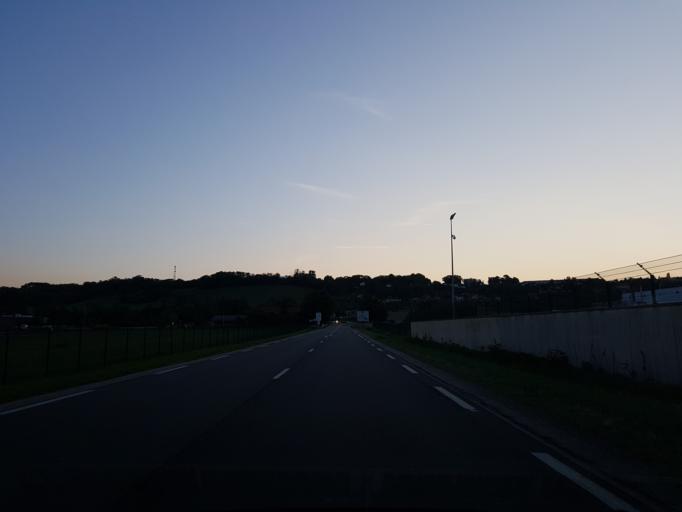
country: FR
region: Champagne-Ardenne
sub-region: Departement de la Haute-Marne
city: Langres
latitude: 47.8557
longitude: 5.3502
